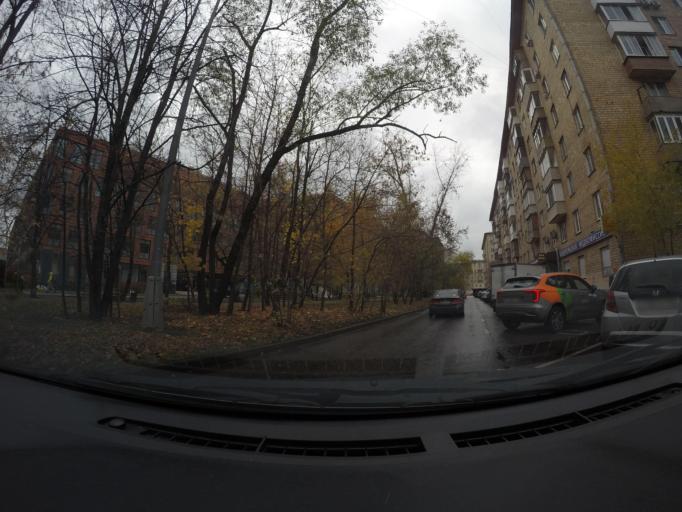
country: RU
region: Moscow
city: Sokol
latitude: 55.8063
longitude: 37.5197
